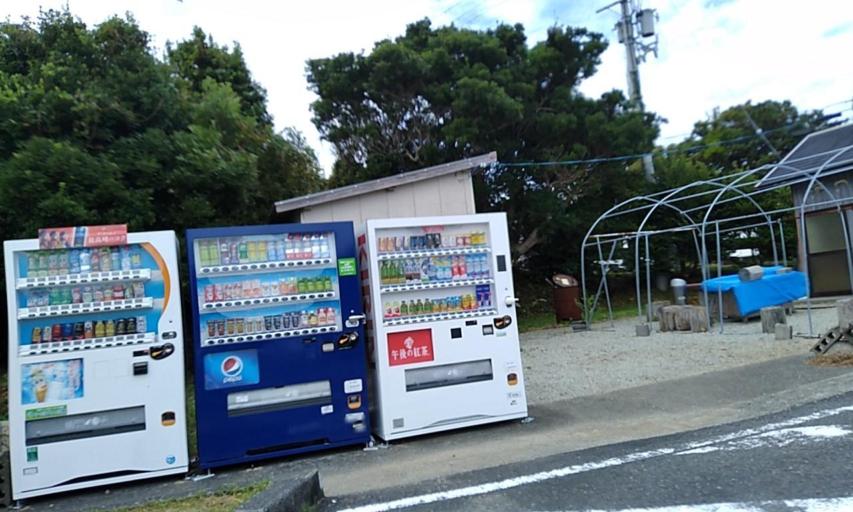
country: JP
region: Wakayama
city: Shingu
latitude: 33.4689
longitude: 135.8568
